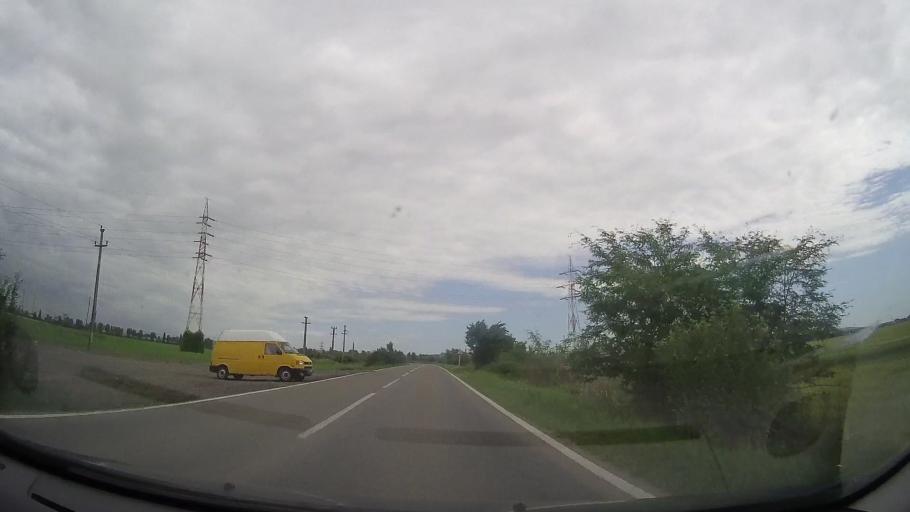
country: RO
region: Prahova
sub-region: Comuna Berceni
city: Berceni
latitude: 44.9308
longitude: 26.1038
